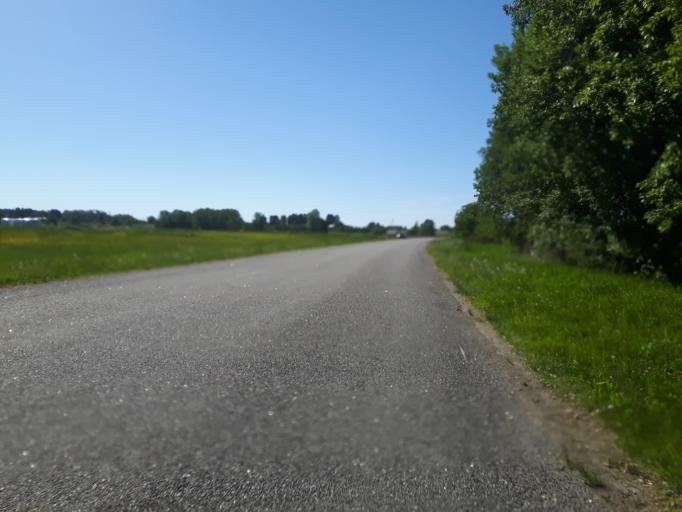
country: EE
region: Laeaene-Virumaa
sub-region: Haljala vald
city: Haljala
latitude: 59.5427
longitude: 26.1871
